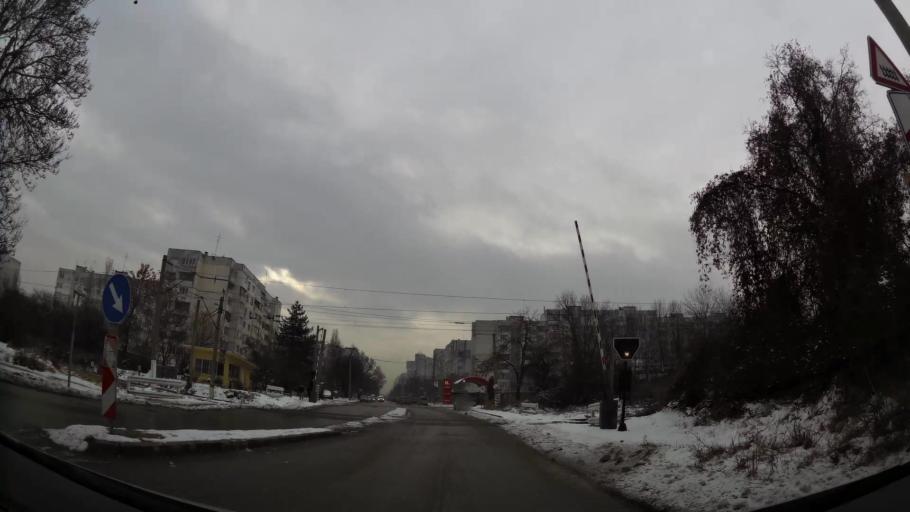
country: BG
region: Sofia-Capital
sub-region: Stolichna Obshtina
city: Sofia
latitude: 42.7152
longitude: 23.2975
